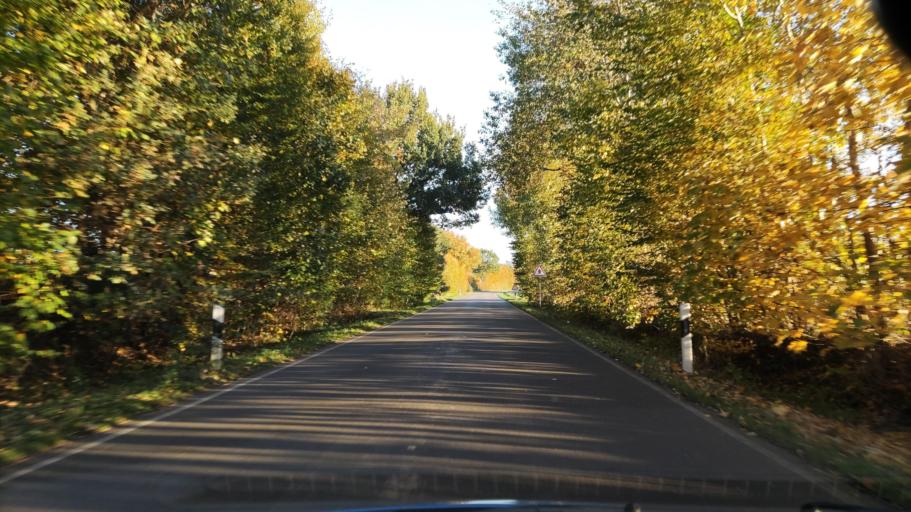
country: DE
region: Schleswig-Holstein
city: Dahmker
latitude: 53.5935
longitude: 10.4509
